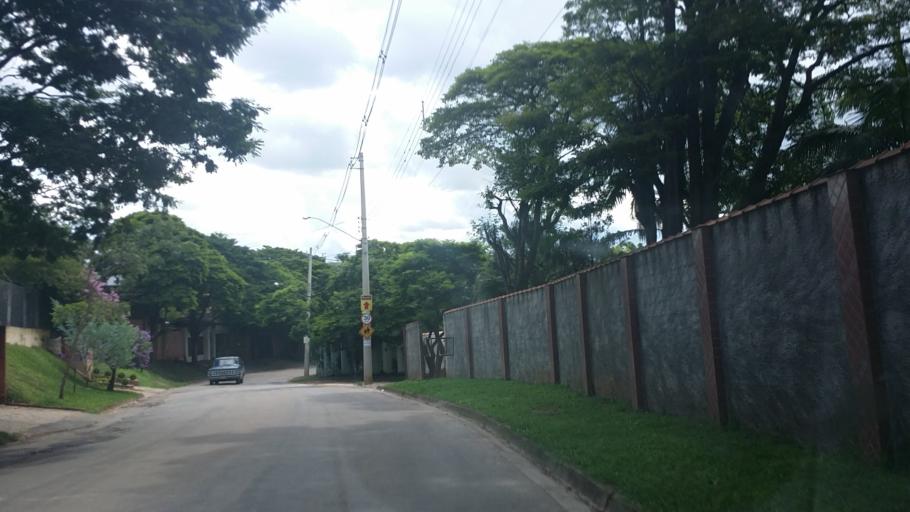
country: BR
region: Sao Paulo
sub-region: Itupeva
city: Itupeva
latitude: -23.1674
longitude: -47.0792
